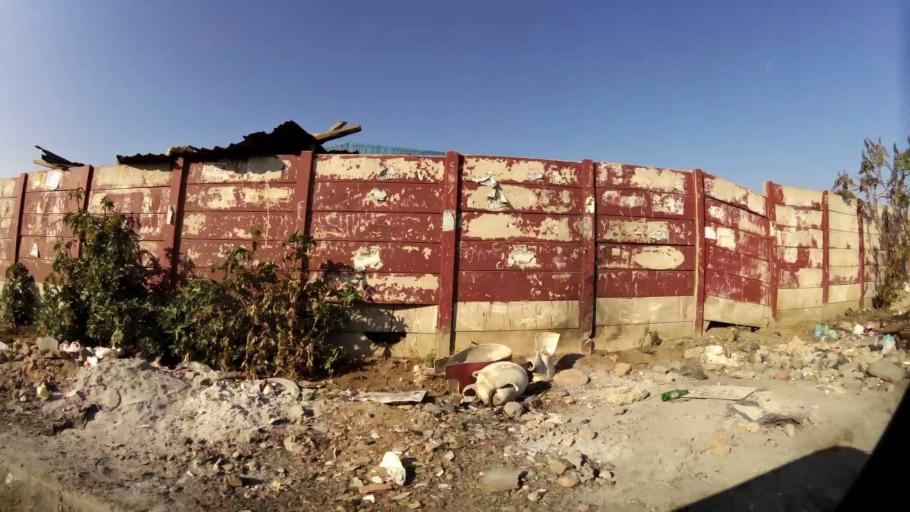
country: ZA
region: Gauteng
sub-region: City of Johannesburg Metropolitan Municipality
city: Soweto
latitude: -26.2575
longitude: 27.9412
